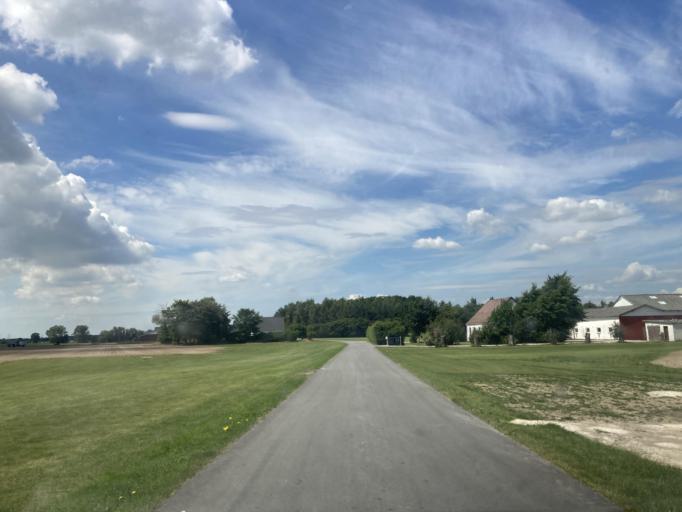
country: DK
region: Zealand
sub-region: Koge Kommune
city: Borup
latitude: 55.4598
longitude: 11.9803
